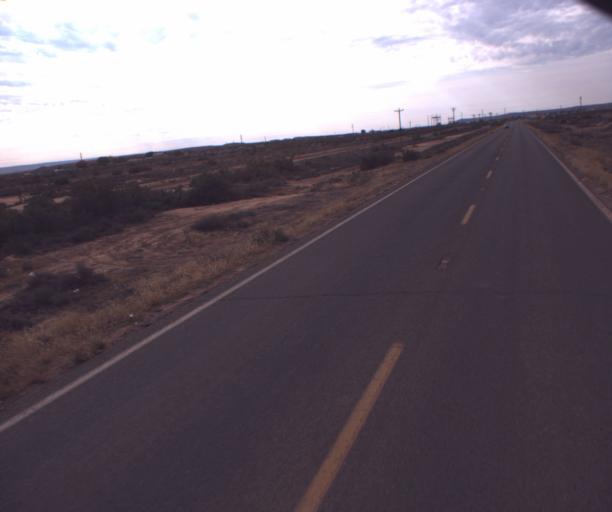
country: US
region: Arizona
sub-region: Apache County
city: Many Farms
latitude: 36.3699
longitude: -109.6132
